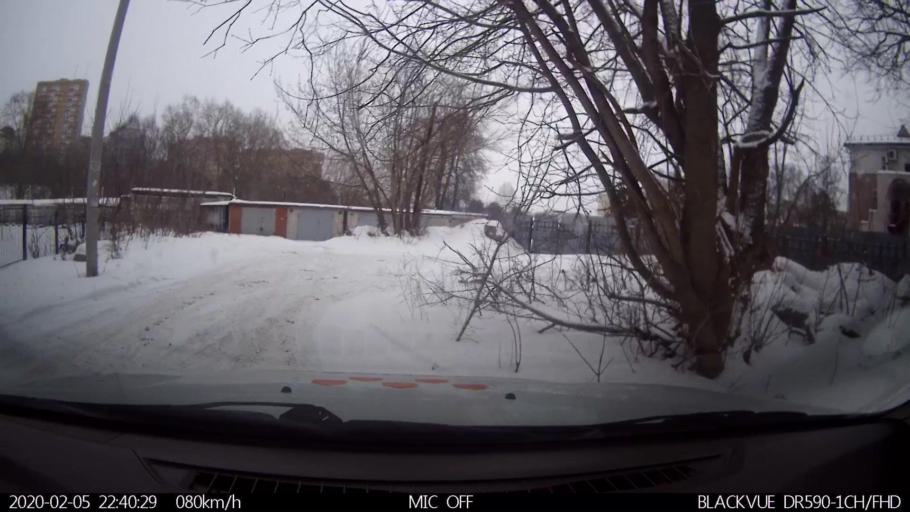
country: RU
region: Nizjnij Novgorod
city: Imeni Stepana Razina
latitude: 54.7222
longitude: 44.3177
